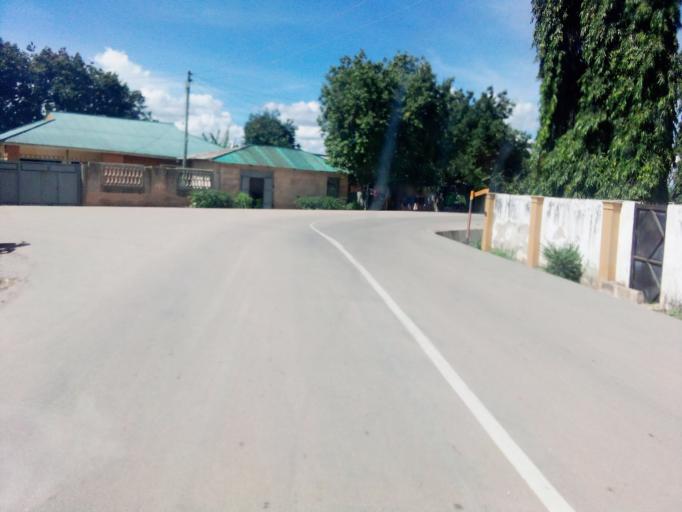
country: TZ
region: Dodoma
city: Dodoma
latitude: -6.1720
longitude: 35.7598
